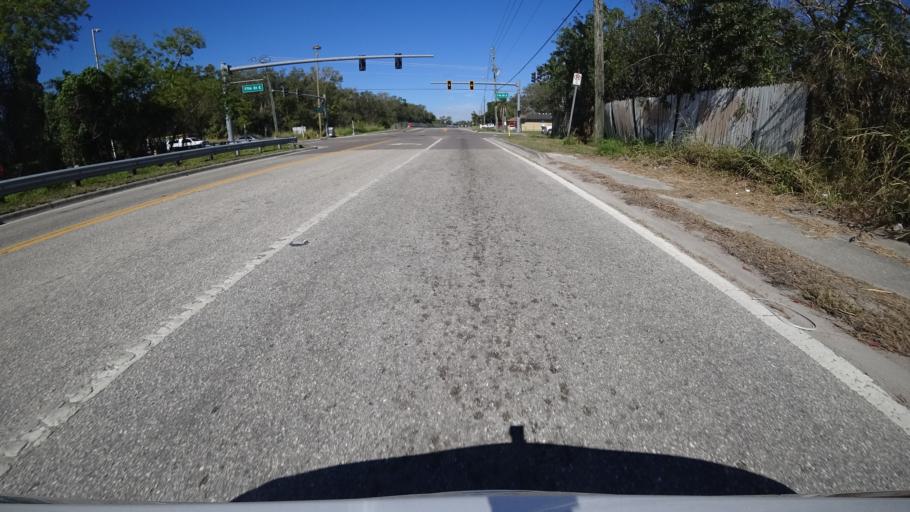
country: US
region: Florida
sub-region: Manatee County
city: Memphis
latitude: 27.5279
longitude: -82.5481
